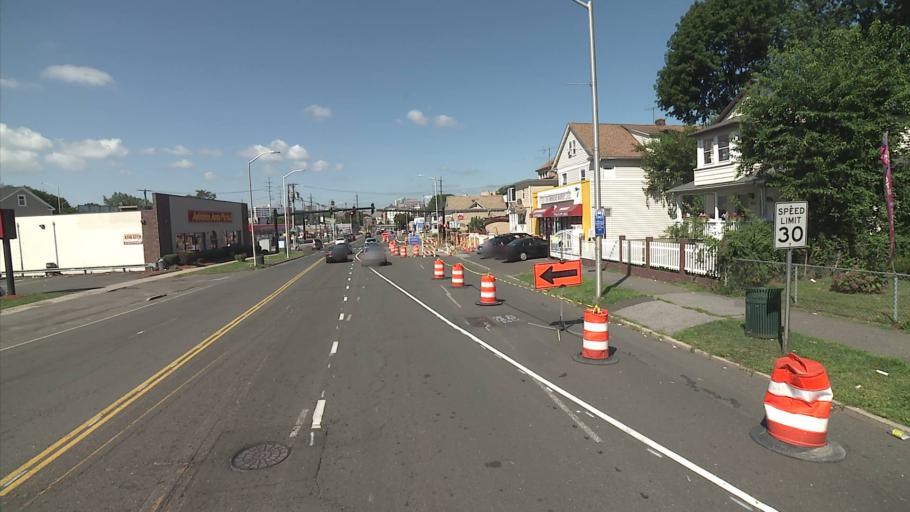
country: US
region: Connecticut
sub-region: Fairfield County
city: Stamford
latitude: 41.0563
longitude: -73.5204
